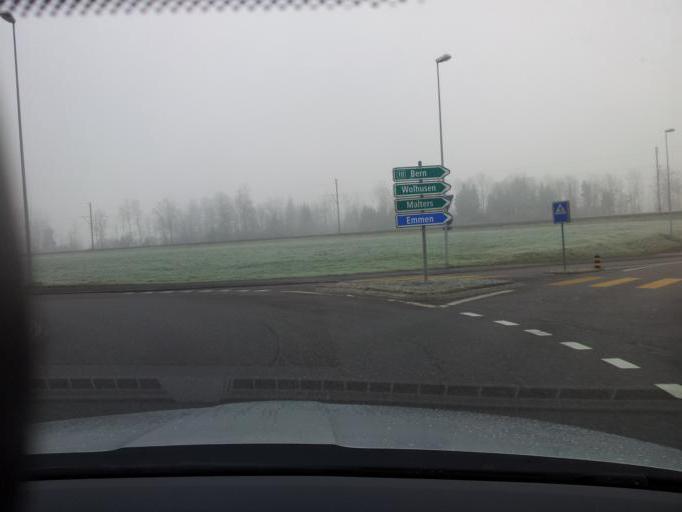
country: CH
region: Lucerne
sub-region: Lucerne-Land District
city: Malters
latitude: 47.0420
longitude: 8.2188
